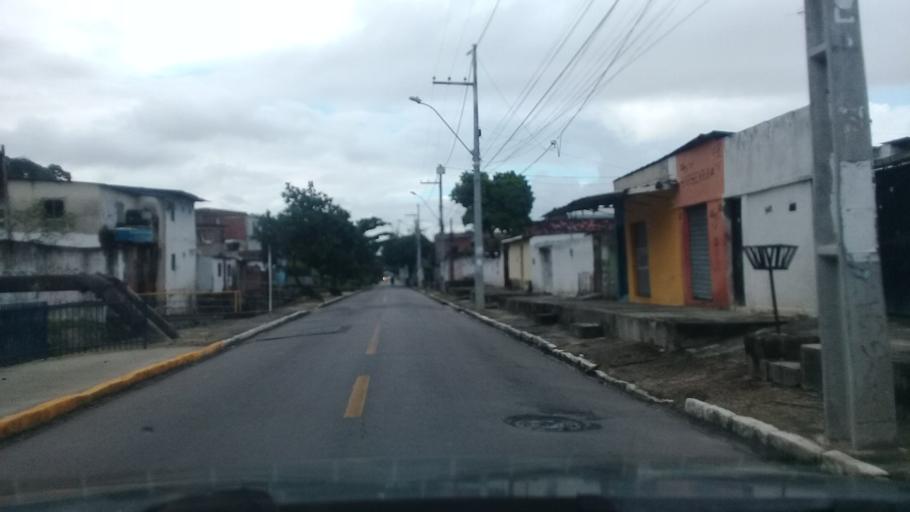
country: BR
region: Pernambuco
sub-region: Jaboatao Dos Guararapes
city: Jaboatao dos Guararapes
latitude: -8.1203
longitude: -34.9507
